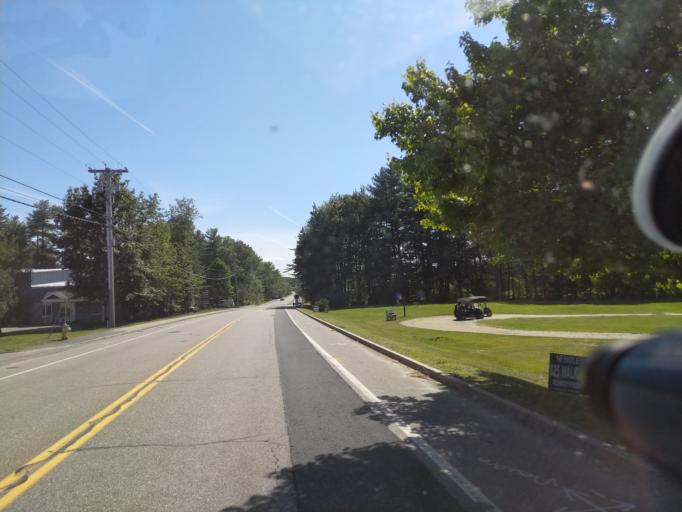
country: US
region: Maine
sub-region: Cumberland County
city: Westbrook
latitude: 43.7100
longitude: -70.3140
